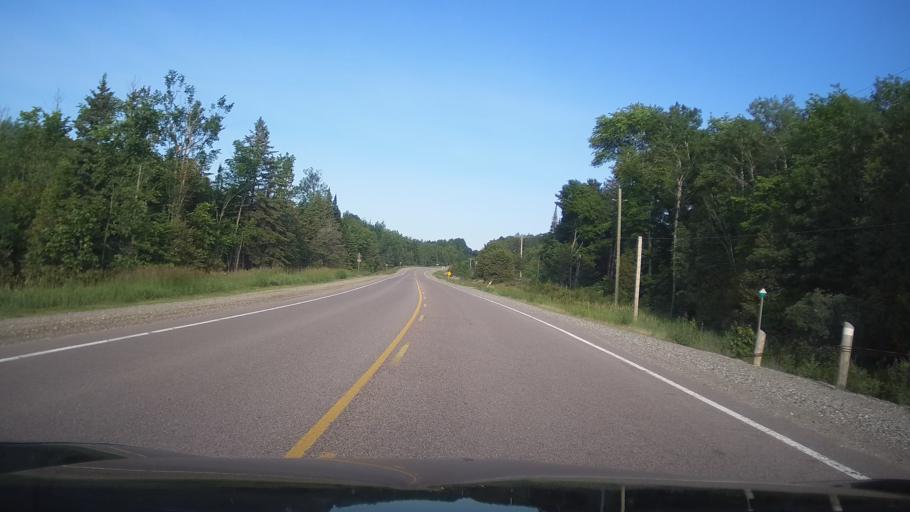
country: CA
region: Ontario
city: Skatepark
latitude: 44.7552
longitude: -76.8659
